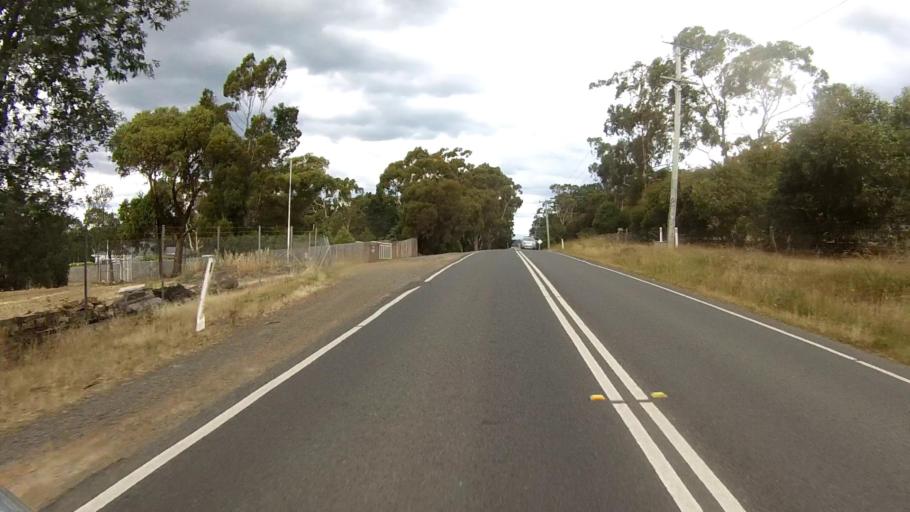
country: AU
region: Tasmania
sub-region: Clarence
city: Cambridge
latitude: -42.8364
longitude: 147.4615
